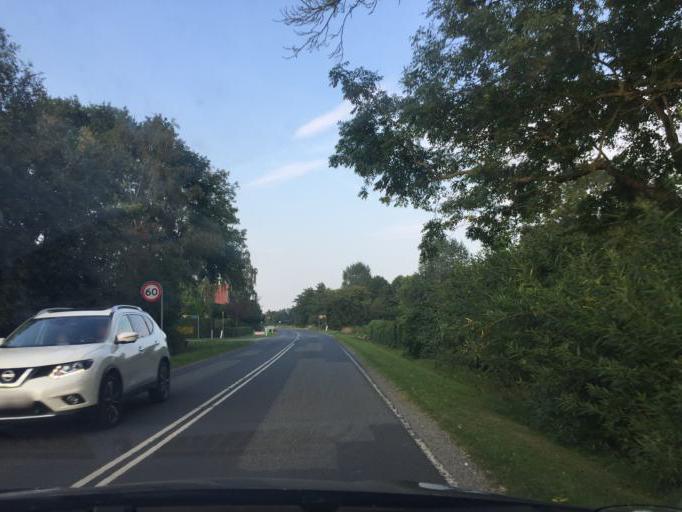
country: DK
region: South Denmark
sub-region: Kerteminde Kommune
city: Langeskov
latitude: 55.2942
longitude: 10.5681
